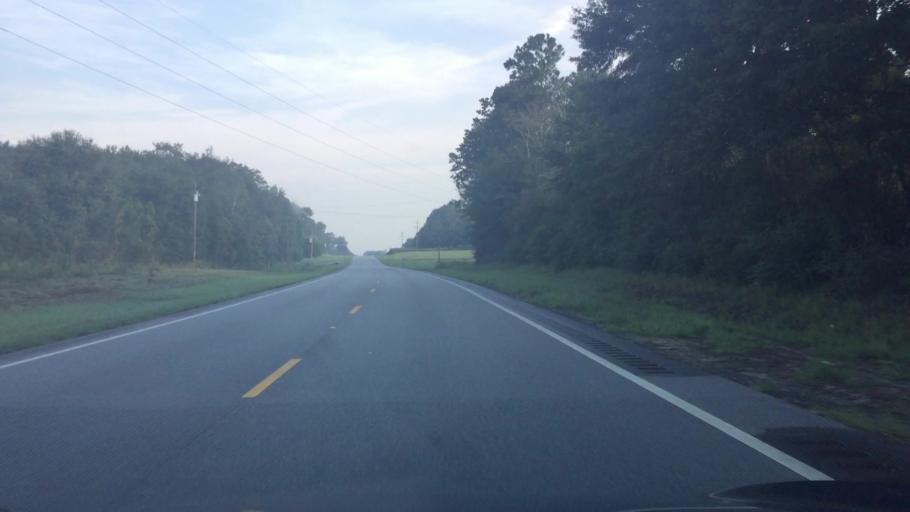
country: US
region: Alabama
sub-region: Covington County
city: Florala
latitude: 31.0734
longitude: -86.4068
